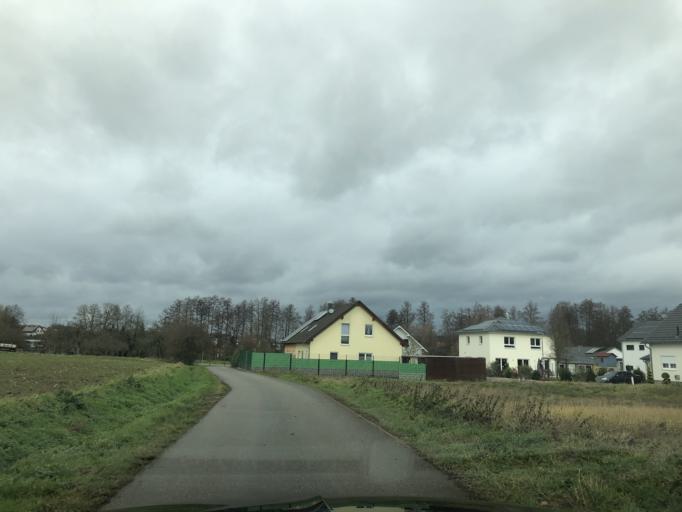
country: DE
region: Baden-Wuerttemberg
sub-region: Karlsruhe Region
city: Bretten
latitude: 49.1175
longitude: 8.7170
